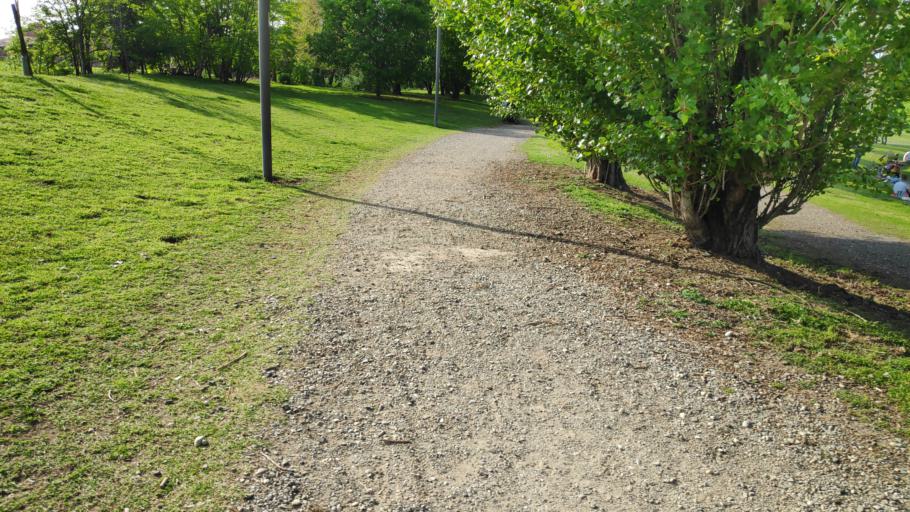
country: IT
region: Lombardy
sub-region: Citta metropolitana di Milano
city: San Giuliano Milanese
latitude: 45.3866
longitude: 9.3059
